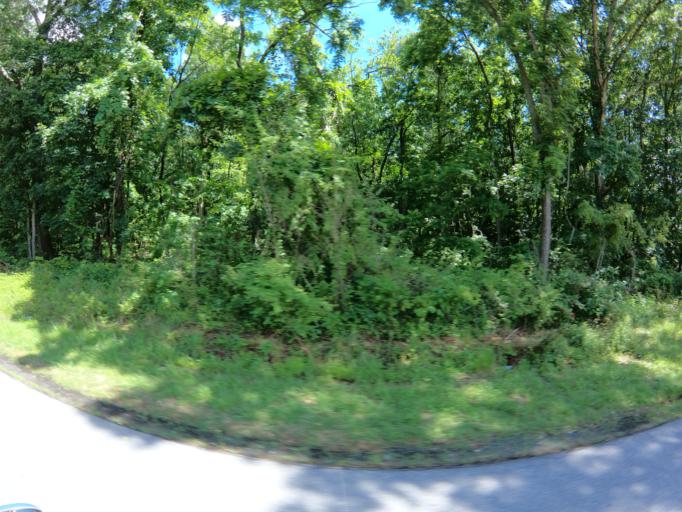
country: US
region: Maryland
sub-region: Queen Anne's County
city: Kingstown
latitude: 39.1178
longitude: -75.9198
